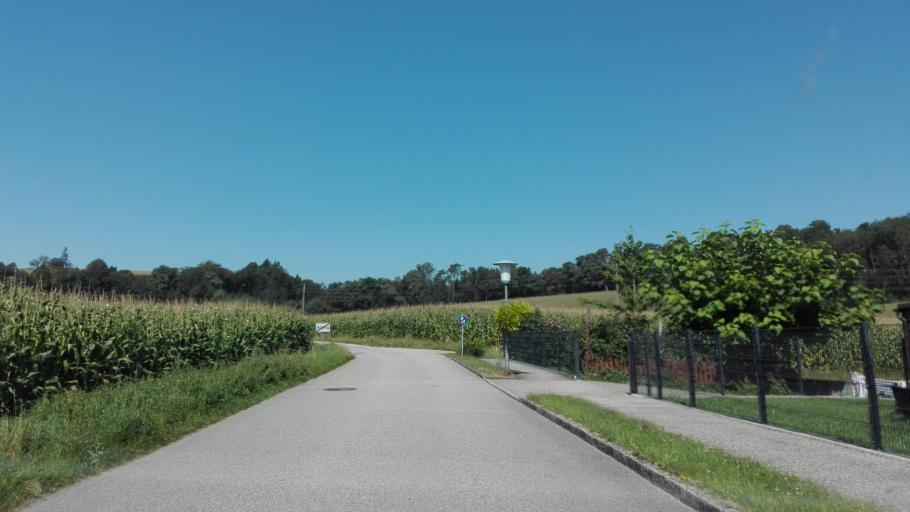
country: AT
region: Upper Austria
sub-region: Politischer Bezirk Perg
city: Perg
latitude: 48.2311
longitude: 14.6919
